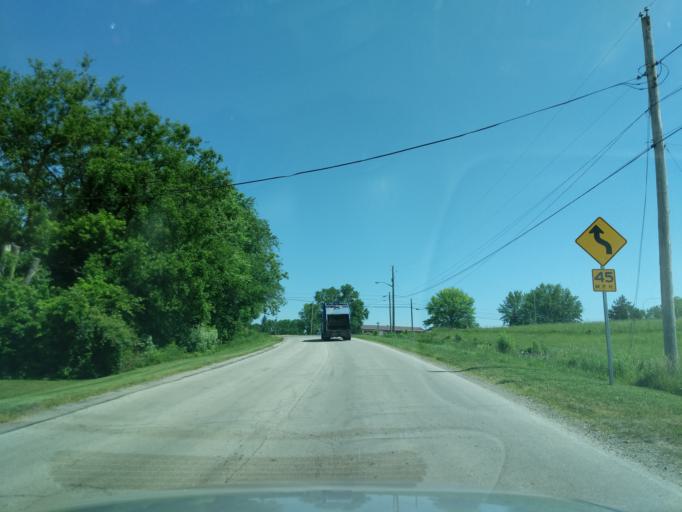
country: US
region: Indiana
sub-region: Huntington County
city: Huntington
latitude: 40.8937
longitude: -85.4843
